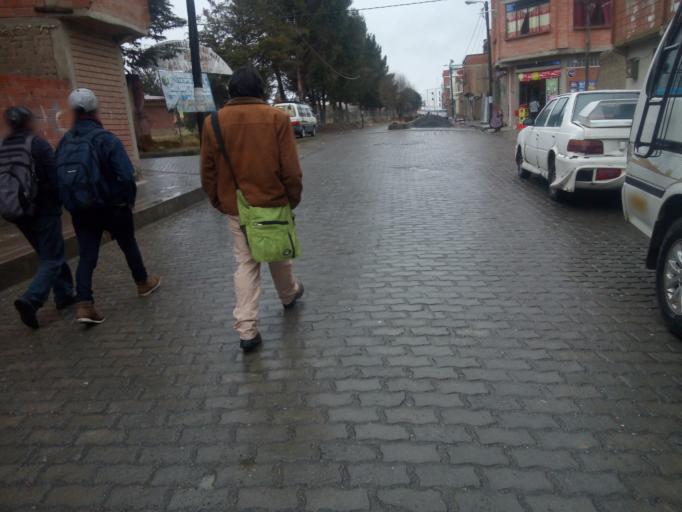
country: BO
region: La Paz
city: Achacachi
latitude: -16.0444
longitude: -68.6902
